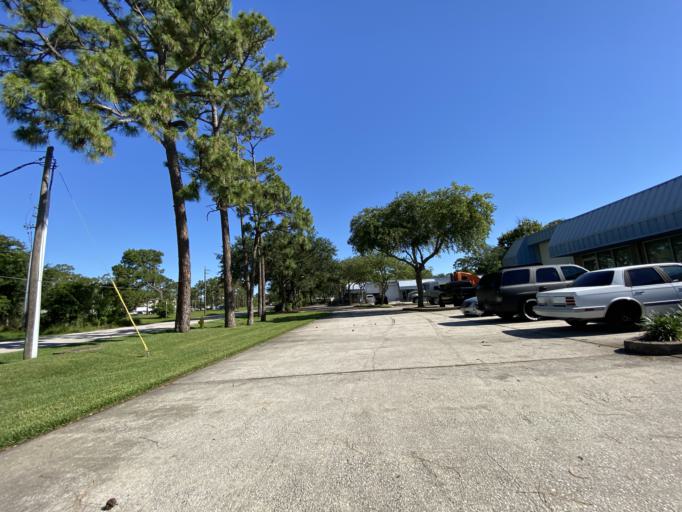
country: US
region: Florida
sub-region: Volusia County
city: Port Orange
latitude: 29.1516
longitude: -80.9942
